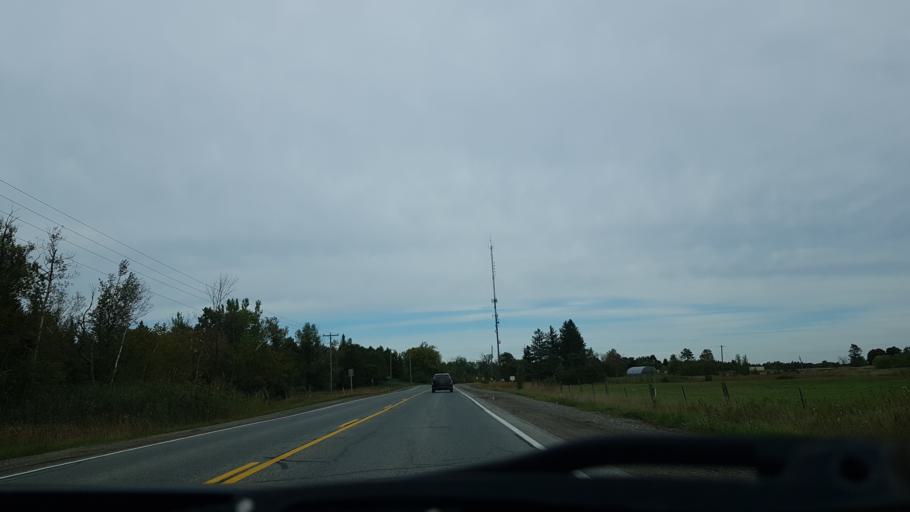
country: CA
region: Ontario
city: Orangeville
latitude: 43.9077
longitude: -79.9438
